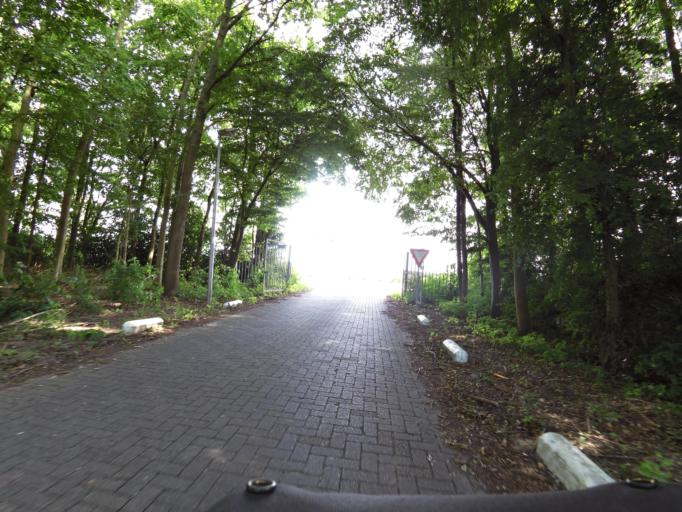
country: NL
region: South Holland
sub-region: Gemeente Goeree-Overflakkee
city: Middelharnis
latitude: 51.7598
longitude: 4.1825
